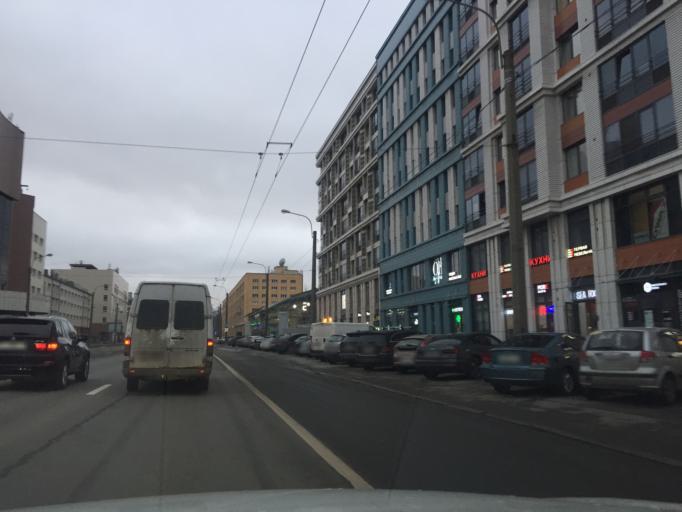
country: RU
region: St.-Petersburg
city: Petrogradka
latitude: 59.9740
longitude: 30.3163
